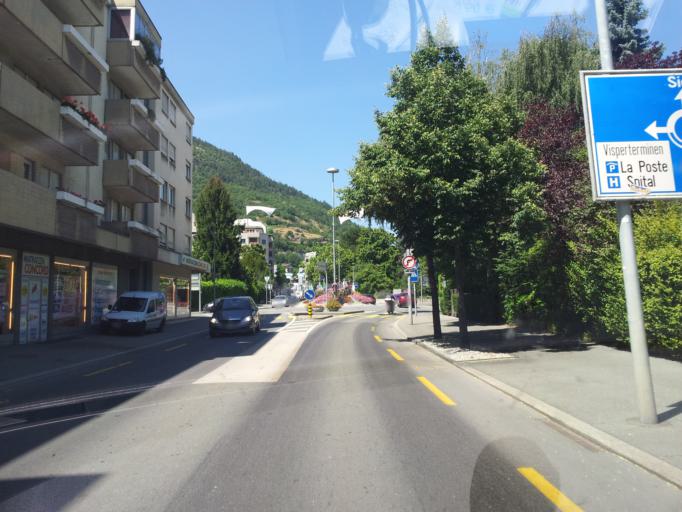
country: CH
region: Valais
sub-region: Visp District
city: Visp
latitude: 46.2921
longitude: 7.8852
